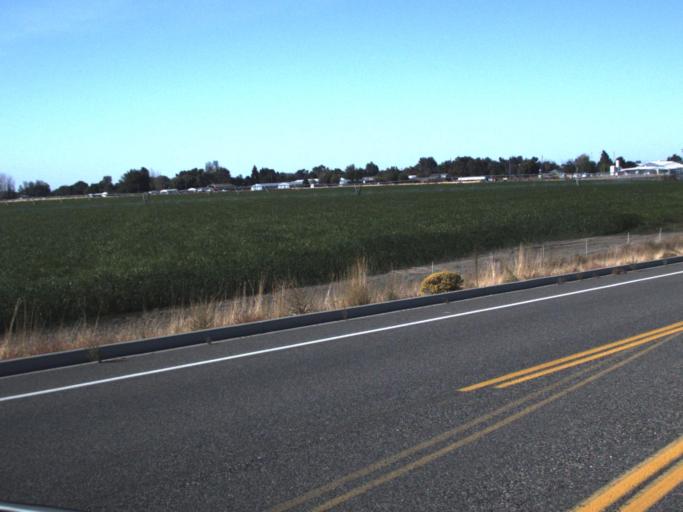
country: US
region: Washington
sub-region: Benton County
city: Finley
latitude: 46.1438
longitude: -119.0127
